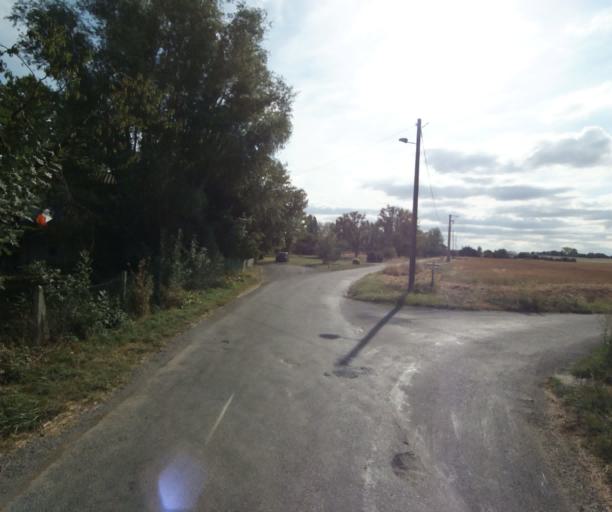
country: FR
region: Midi-Pyrenees
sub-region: Departement du Tarn
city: Puylaurens
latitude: 43.5262
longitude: 2.0028
